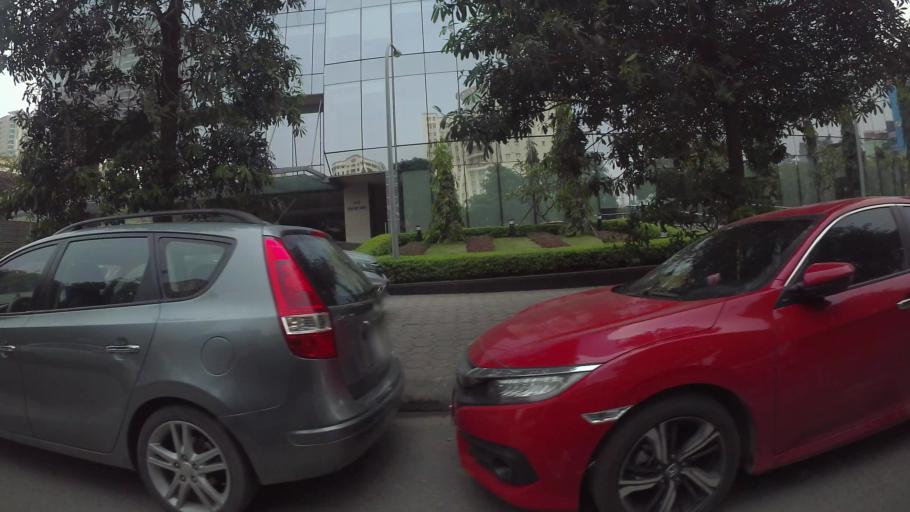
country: VN
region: Ha Noi
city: Thanh Xuan
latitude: 21.0088
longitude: 105.7984
